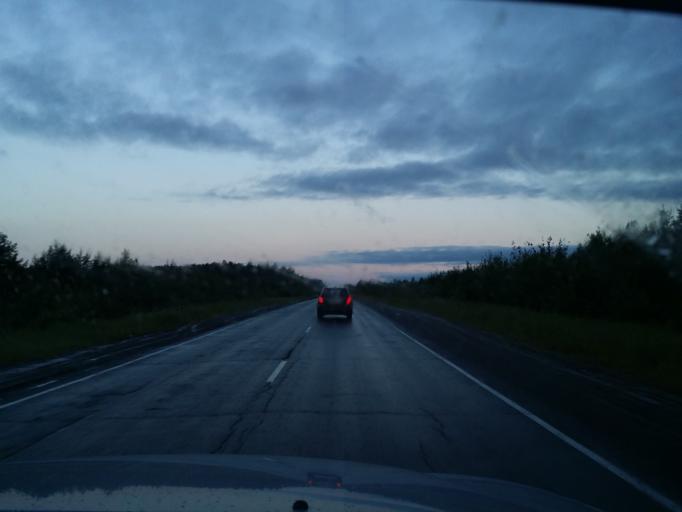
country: RU
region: Khanty-Mansiyskiy Avtonomnyy Okrug
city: Salym
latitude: 60.2247
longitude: 71.8666
